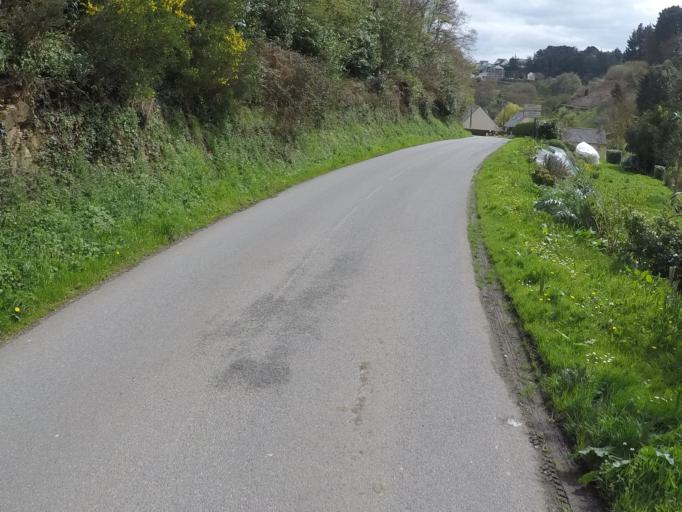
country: FR
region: Brittany
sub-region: Departement des Cotes-d'Armor
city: Plouezec
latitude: 48.7308
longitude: -2.9512
